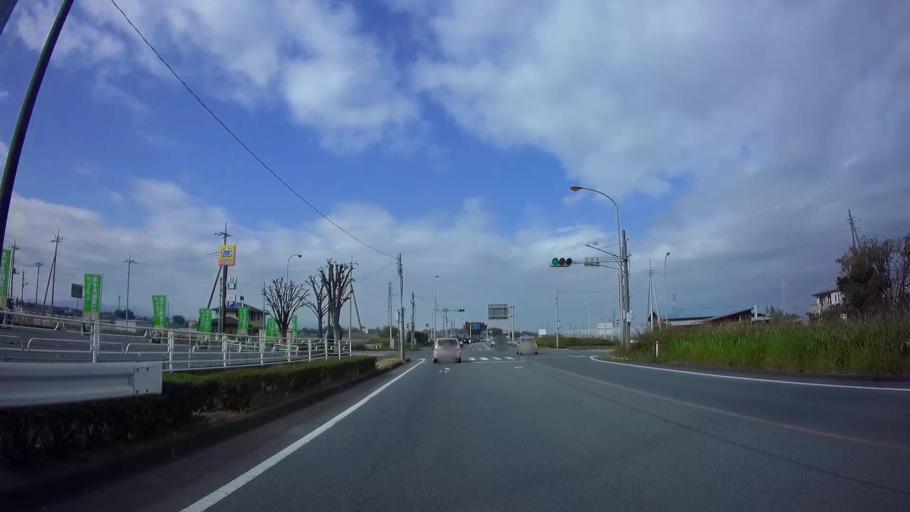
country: JP
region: Saitama
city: Fukayacho
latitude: 36.2167
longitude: 139.2551
